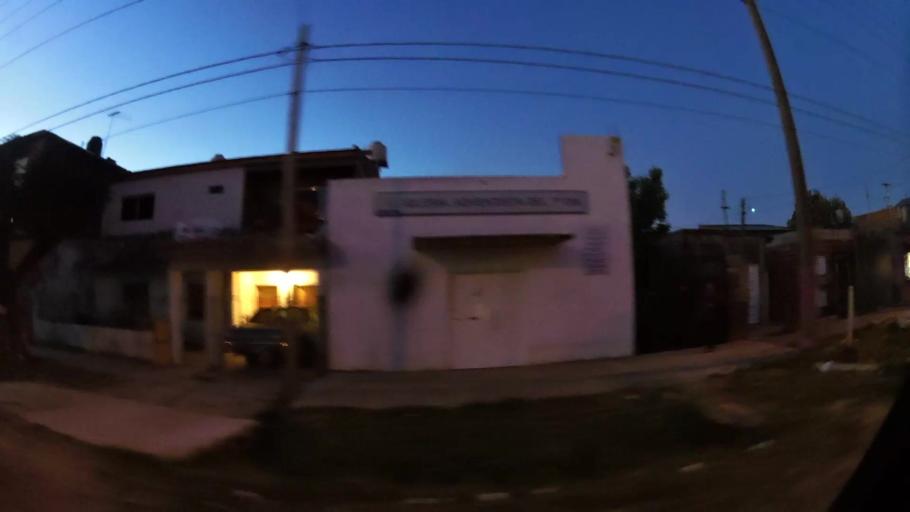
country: AR
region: Buenos Aires
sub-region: Partido de Almirante Brown
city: Adrogue
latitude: -34.7533
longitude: -58.3357
